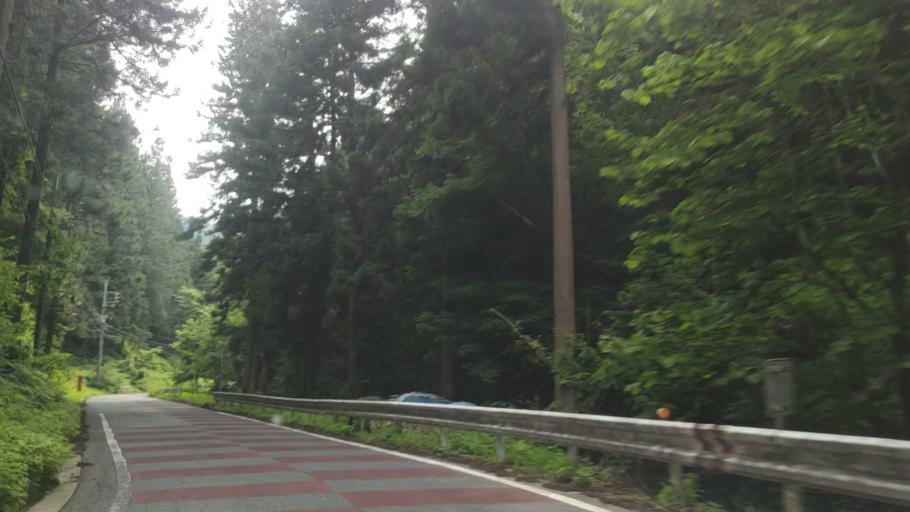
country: JP
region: Gunma
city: Tomioka
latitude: 36.1437
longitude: 138.7291
